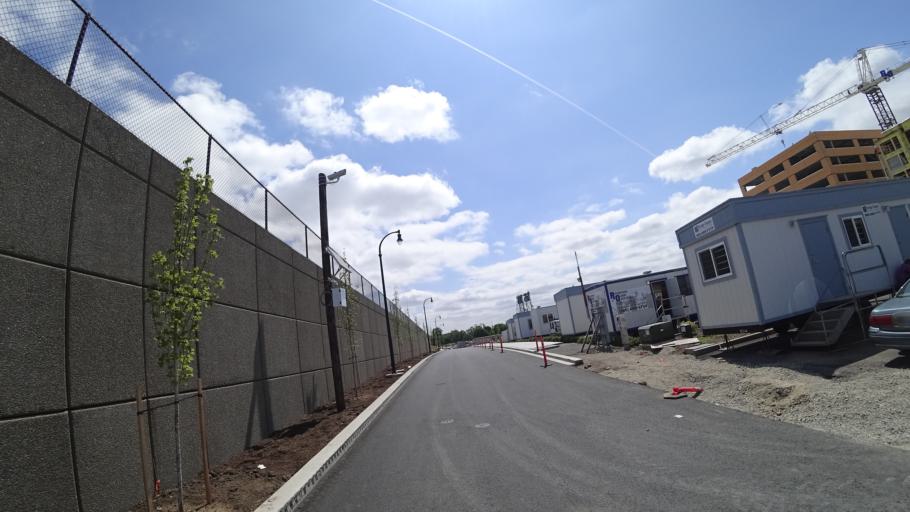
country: US
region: Washington
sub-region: Clark County
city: Vancouver
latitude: 45.6250
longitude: -122.6784
